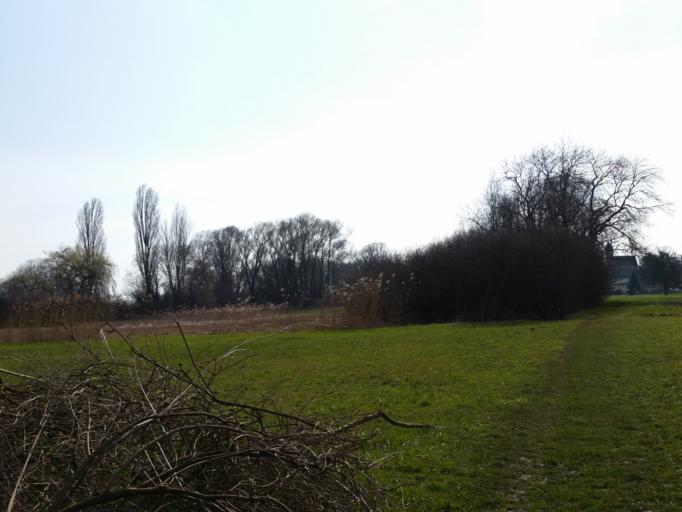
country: CH
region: Thurgau
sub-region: Arbon District
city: Egnach
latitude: 47.5515
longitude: 9.3807
